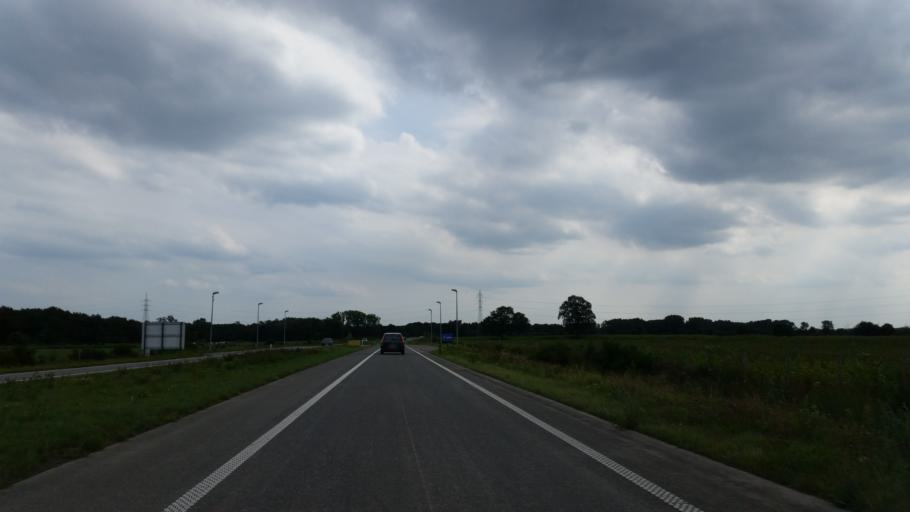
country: BE
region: Flanders
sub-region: Provincie Antwerpen
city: Kasterlee
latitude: 51.2276
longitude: 4.9623
